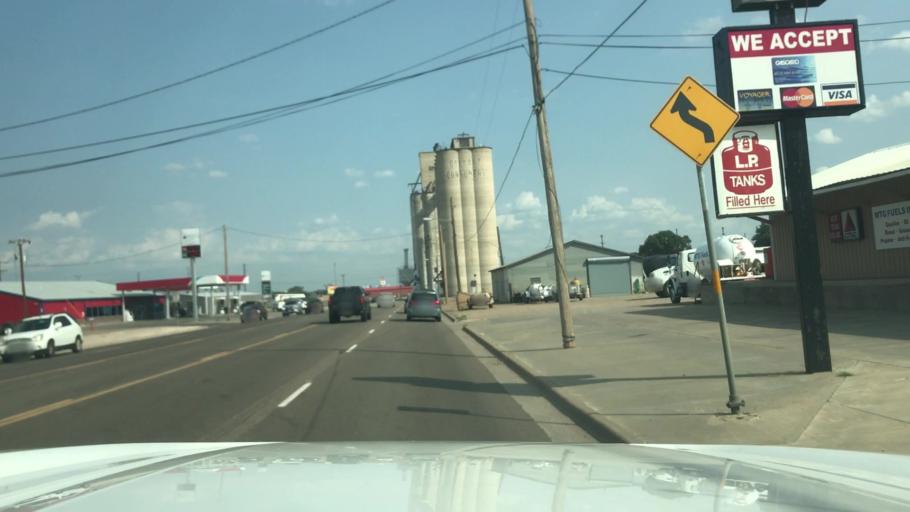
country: US
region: Texas
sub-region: Dallam County
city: Dalhart
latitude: 36.0689
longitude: -102.5273
